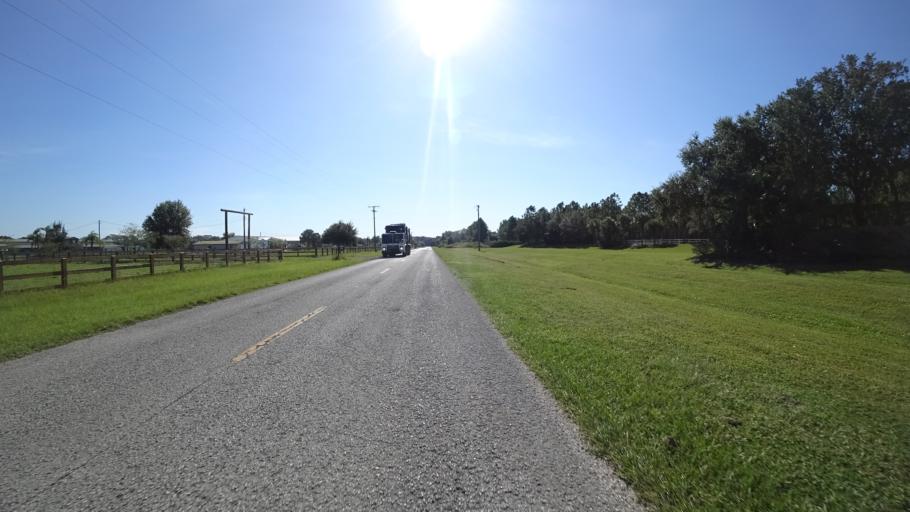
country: US
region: Florida
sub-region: Hillsborough County
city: Wimauma
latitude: 27.6576
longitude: -82.3244
